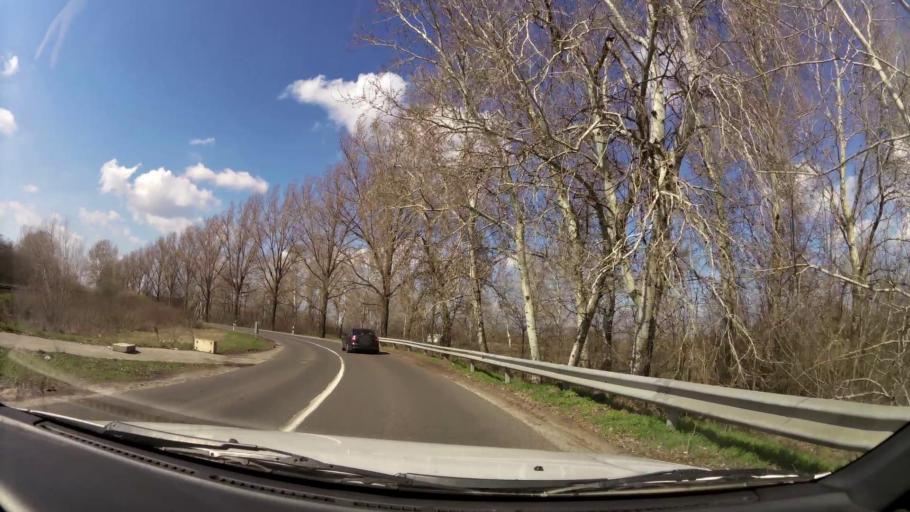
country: HU
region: Pest
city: Farmos
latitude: 47.3740
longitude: 19.7972
